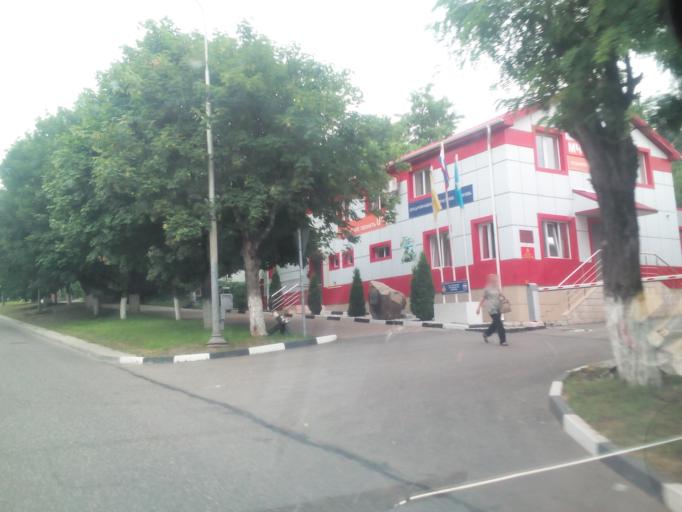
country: RU
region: Stavropol'skiy
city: Zheleznovodsk
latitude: 44.1327
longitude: 43.0350
